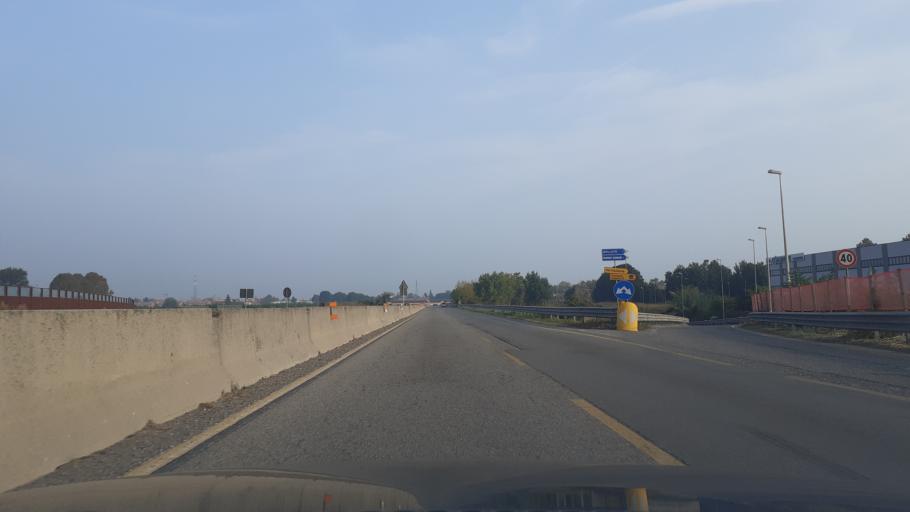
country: IT
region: Lombardy
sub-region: Citta metropolitana di Milano
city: Cormano
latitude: 45.5486
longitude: 9.1475
